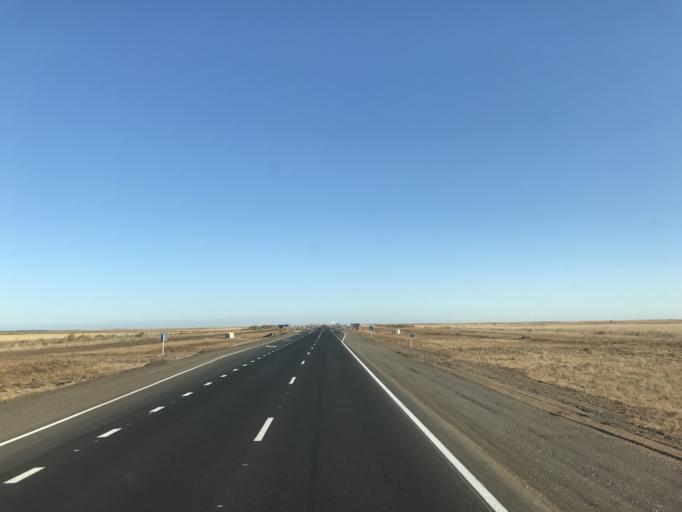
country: KZ
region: Pavlodar
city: Kurchatov
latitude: 51.2562
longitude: 78.5591
